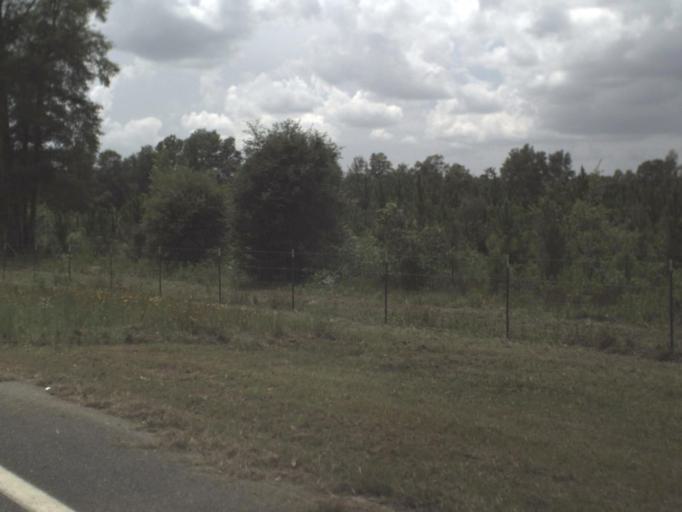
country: US
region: Florida
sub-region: Madison County
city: Madison
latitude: 30.4772
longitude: -83.2557
